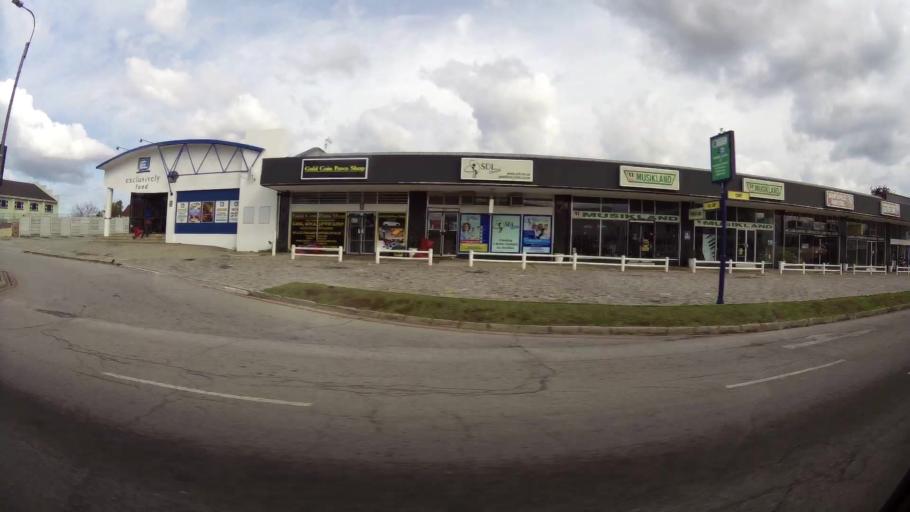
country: ZA
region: Eastern Cape
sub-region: Nelson Mandela Bay Metropolitan Municipality
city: Port Elizabeth
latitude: -33.9488
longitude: 25.5656
